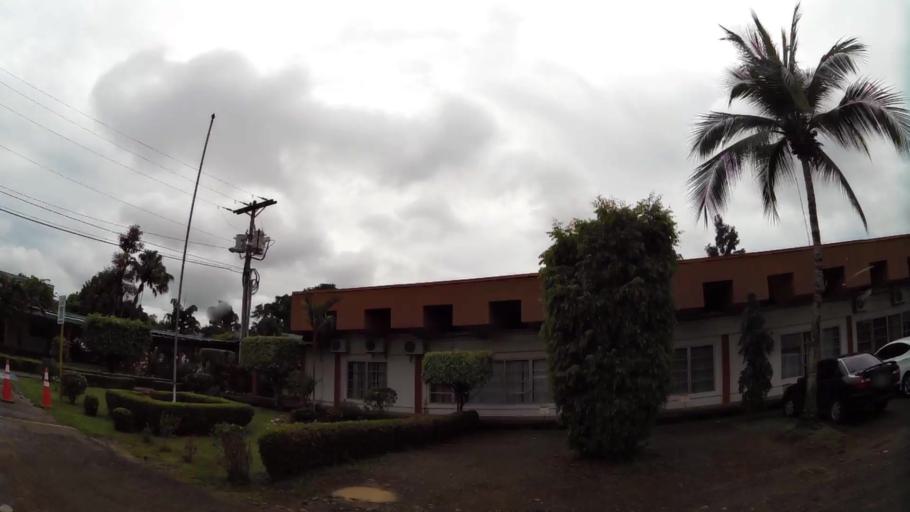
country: PA
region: Chiriqui
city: David
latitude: 8.4234
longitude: -82.4426
